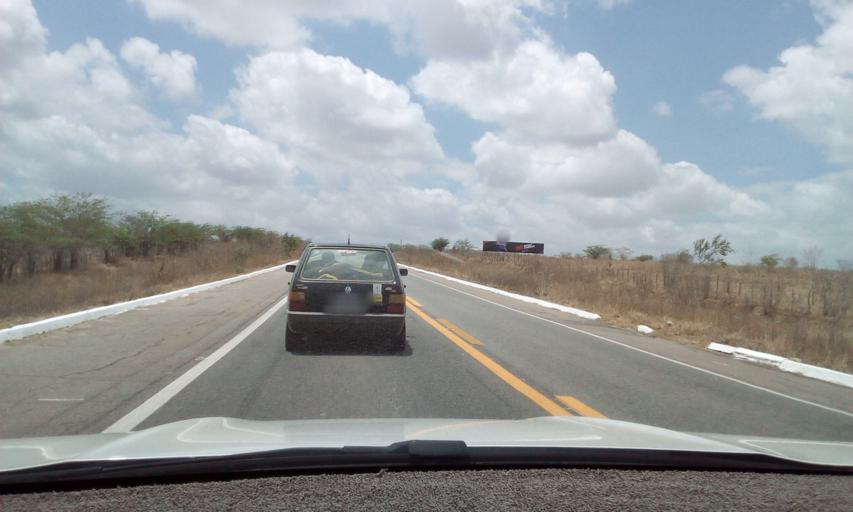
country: BR
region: Pernambuco
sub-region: Taquaritinga Do Norte
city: Taquaritinga do Norte
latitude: -7.7246
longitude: -36.0743
